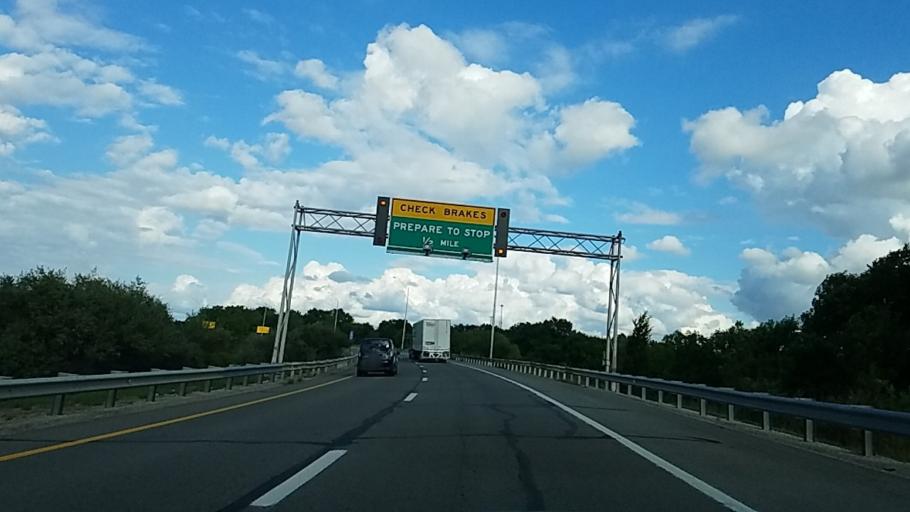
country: US
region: Ohio
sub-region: Lorain County
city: North Ridgeville
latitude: 41.3776
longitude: -82.0001
